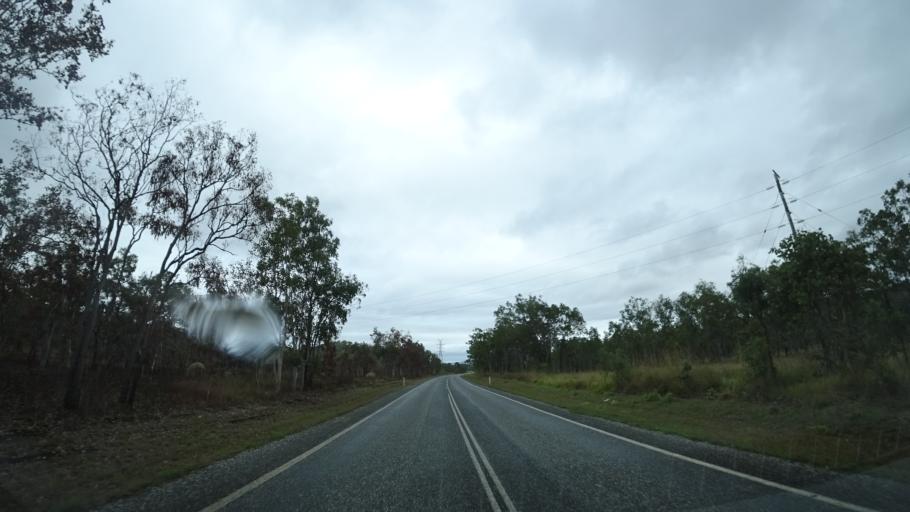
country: AU
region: Queensland
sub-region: Tablelands
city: Mareeba
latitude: -16.7368
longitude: 145.3501
